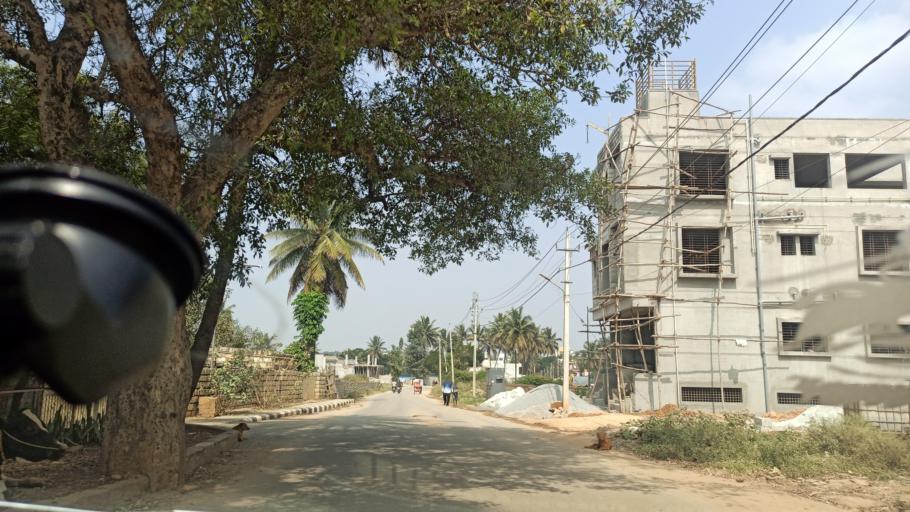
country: IN
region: Karnataka
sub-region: Bangalore Urban
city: Yelahanka
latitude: 13.0838
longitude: 77.6182
